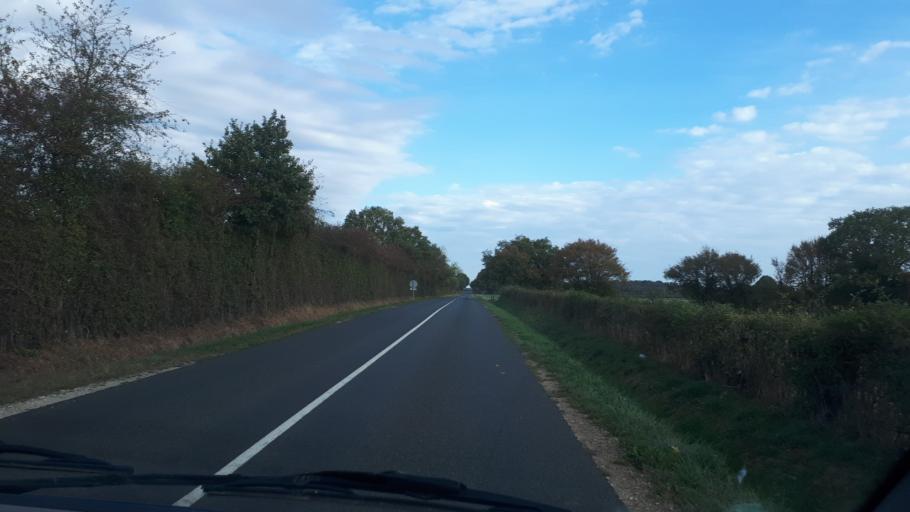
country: FR
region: Centre
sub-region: Departement du Loir-et-Cher
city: Mondoubleau
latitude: 47.9350
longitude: 0.9336
